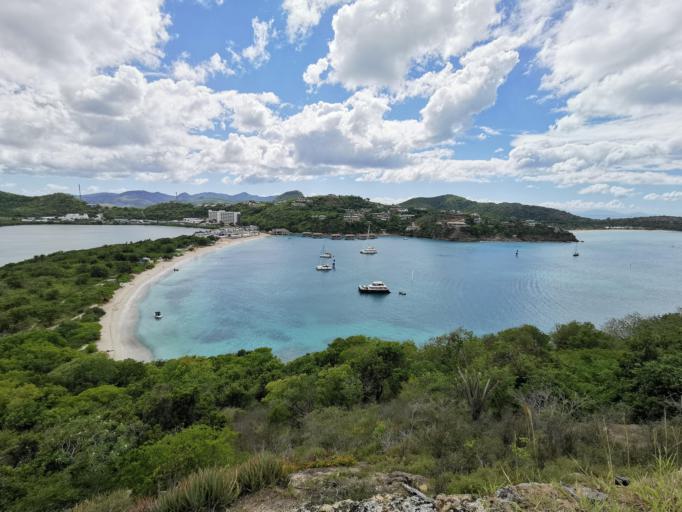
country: AG
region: Saint John
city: Saint John's
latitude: 17.1296
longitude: -61.8864
